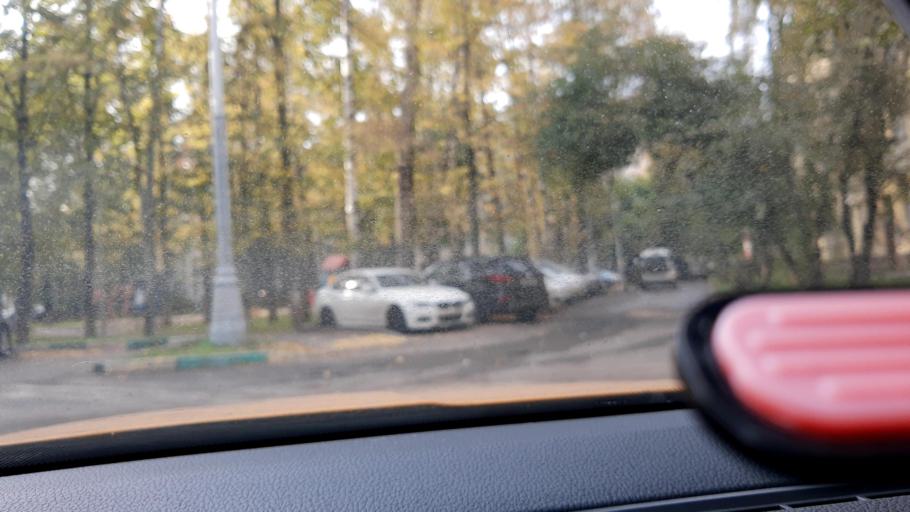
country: RU
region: Moscow
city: Novyye Cheremushki
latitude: 55.6911
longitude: 37.5882
